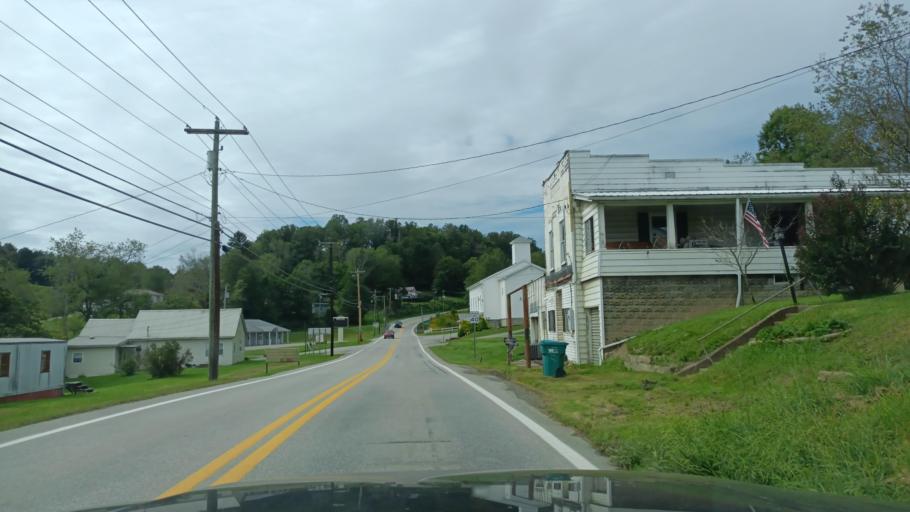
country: US
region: West Virginia
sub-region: Taylor County
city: Grafton
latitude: 39.3335
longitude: -80.0802
